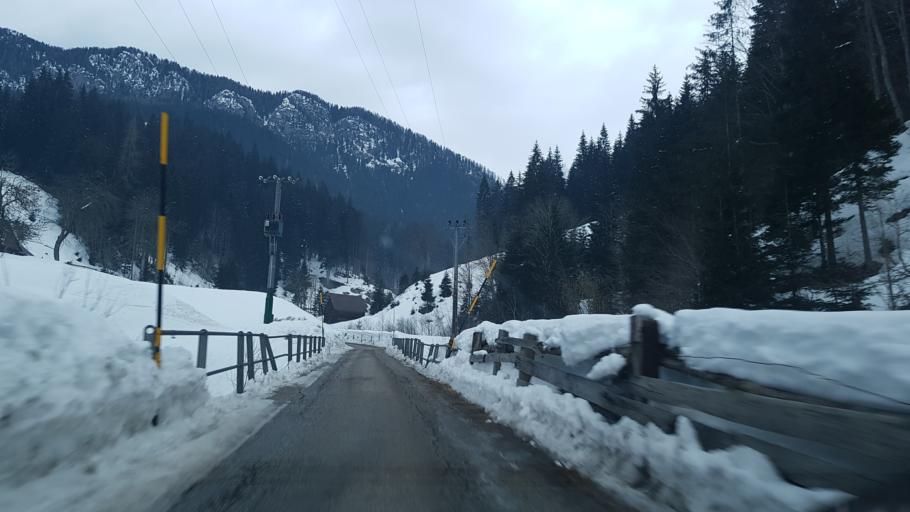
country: IT
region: Friuli Venezia Giulia
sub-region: Provincia di Udine
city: Malborghetto
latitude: 46.5426
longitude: 13.4751
